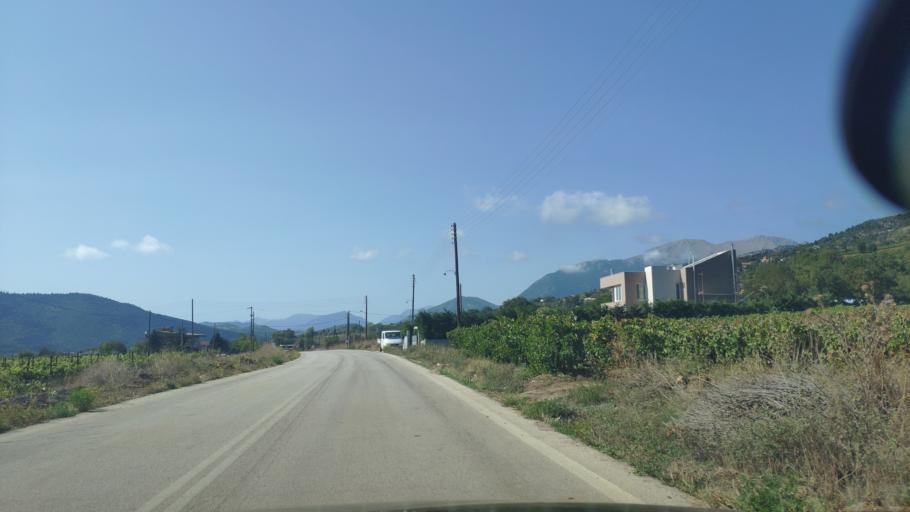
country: GR
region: Peloponnese
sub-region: Nomos Korinthias
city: Xylokastro
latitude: 37.9575
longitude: 22.5778
